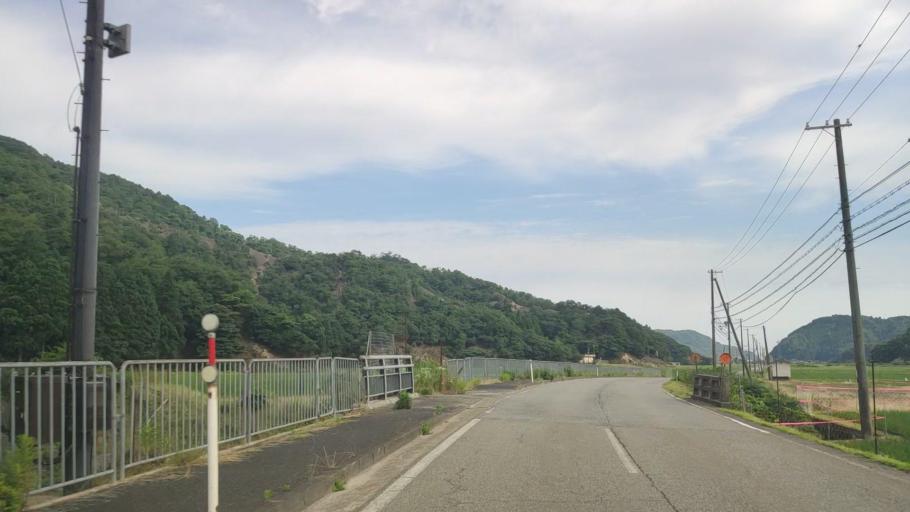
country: JP
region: Hyogo
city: Toyooka
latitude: 35.6208
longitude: 134.8415
